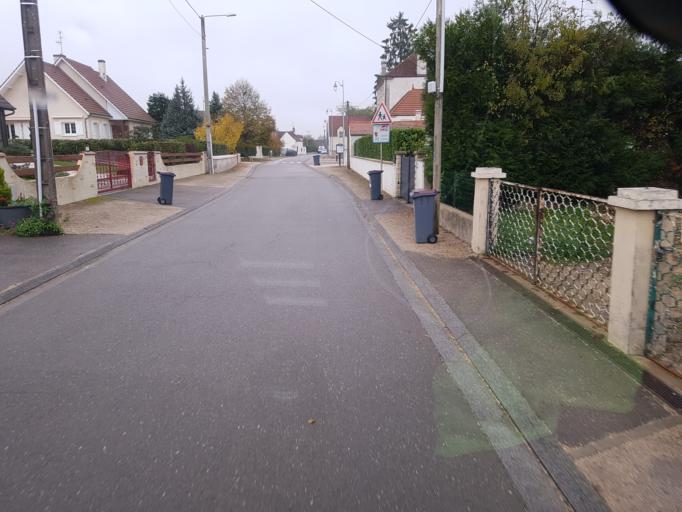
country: FR
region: Bourgogne
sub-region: Departement de la Cote-d'Or
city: Genlis
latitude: 47.2788
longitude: 5.2205
